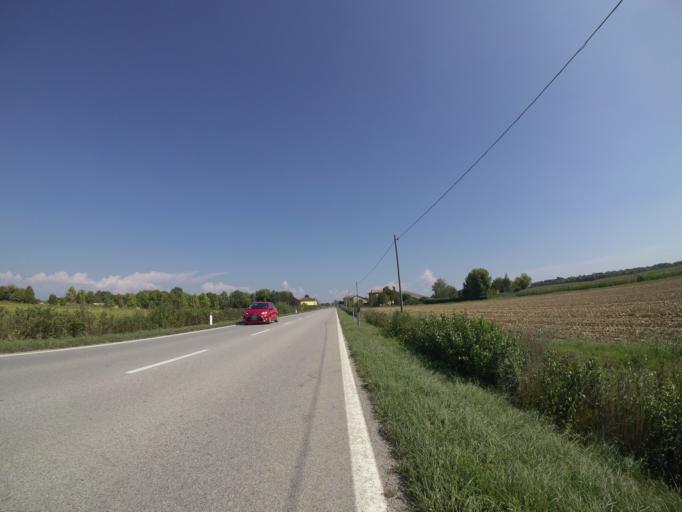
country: IT
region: Friuli Venezia Giulia
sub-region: Provincia di Udine
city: Muzzana del Turgnano
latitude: 45.8141
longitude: 13.1504
